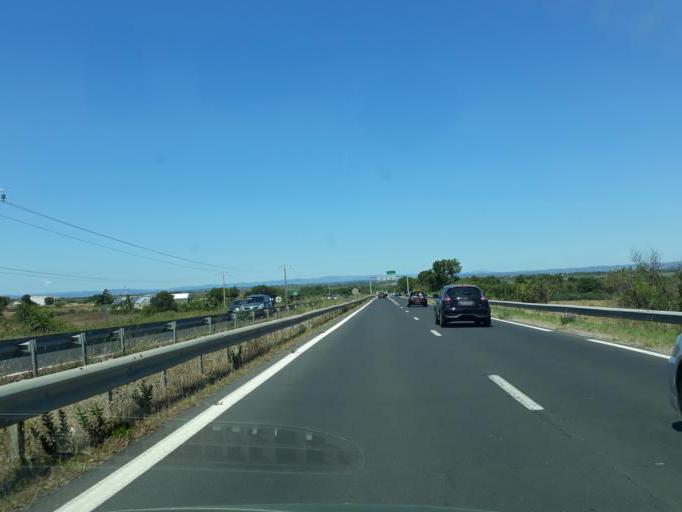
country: FR
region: Languedoc-Roussillon
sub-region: Departement de l'Herault
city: Le Cap d'Agde
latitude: 43.3028
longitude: 3.5078
